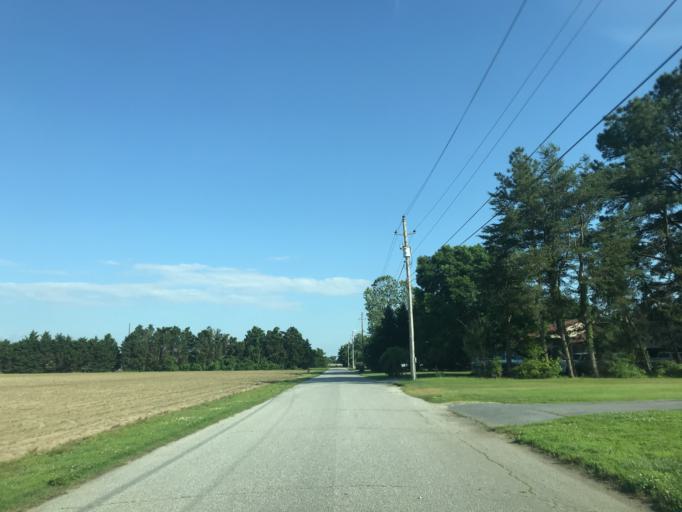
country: US
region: Maryland
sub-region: Wicomico County
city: Hebron
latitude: 38.5385
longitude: -75.7140
